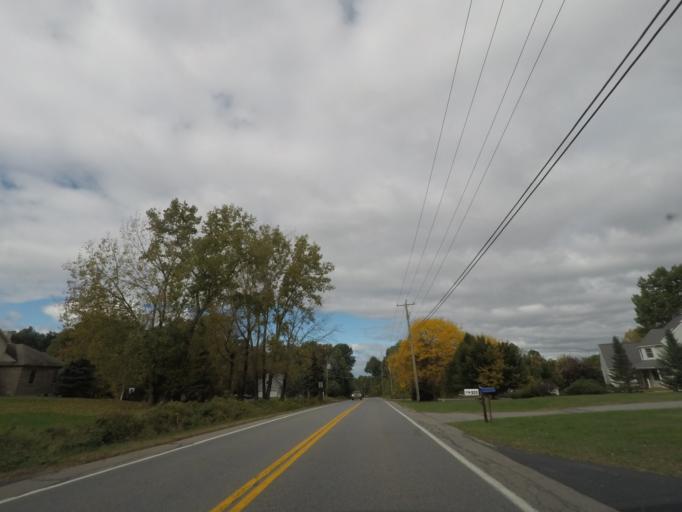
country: US
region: New York
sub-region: Saratoga County
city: Country Knolls
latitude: 42.8868
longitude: -73.7675
